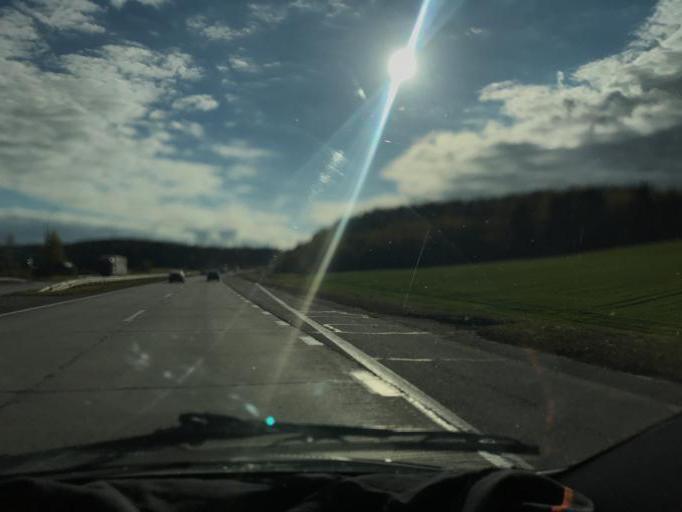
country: BY
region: Minsk
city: Lahoysk
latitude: 54.1144
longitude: 27.8050
